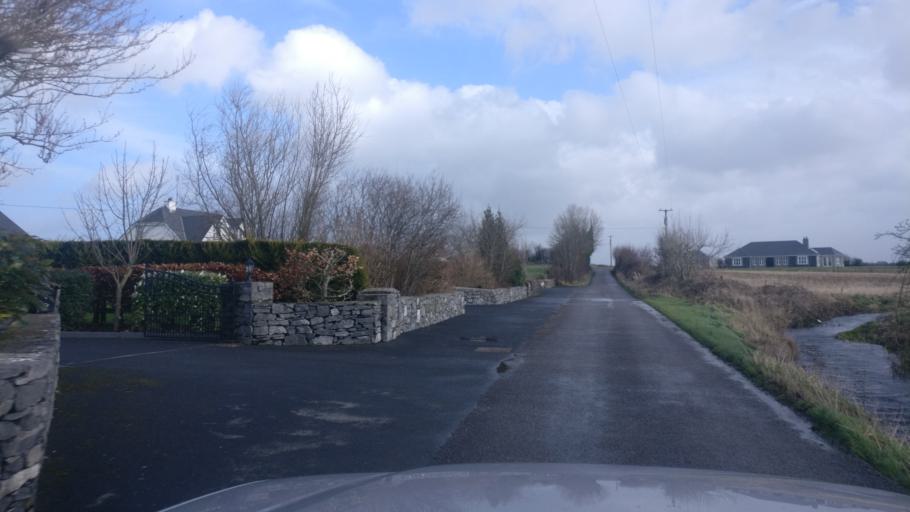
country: IE
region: Connaught
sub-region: County Galway
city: Loughrea
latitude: 53.2596
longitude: -8.5833
